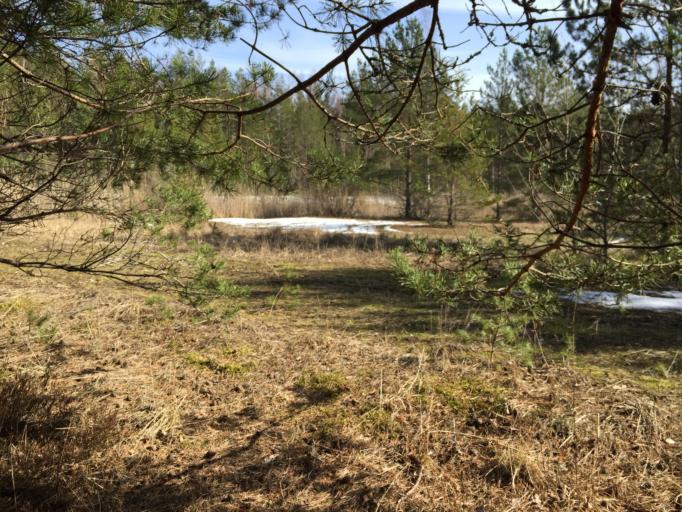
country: EE
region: Paernumaa
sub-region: Paernu linn
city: Parnu
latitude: 58.2325
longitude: 24.5196
